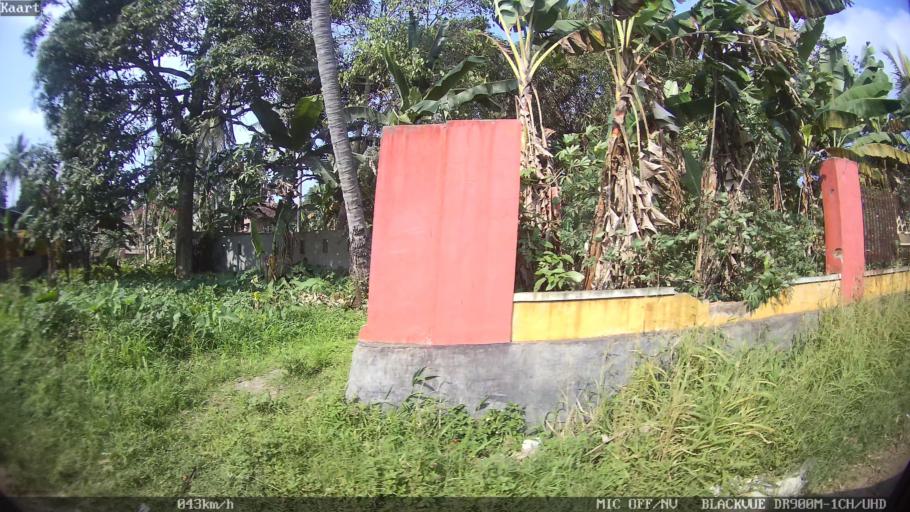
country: ID
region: Lampung
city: Kedaton
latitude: -5.3802
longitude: 105.1974
